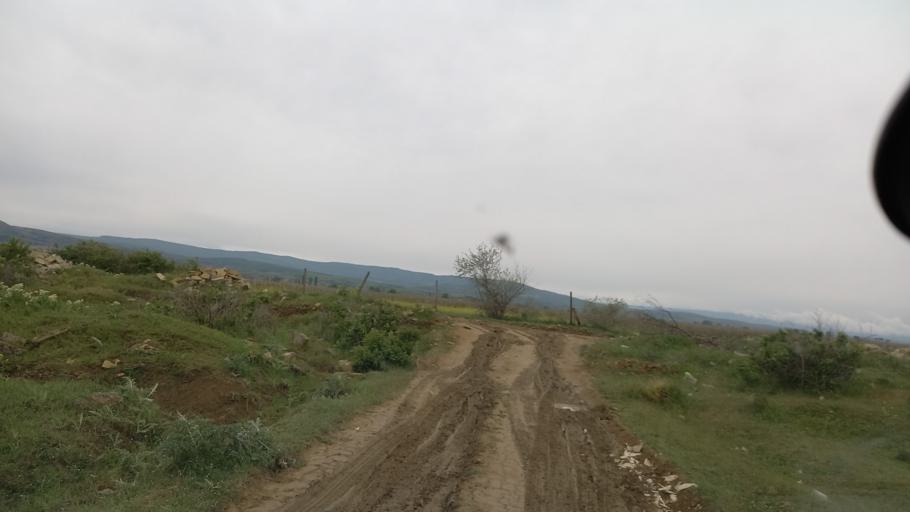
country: RU
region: Dagestan
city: Sabnova
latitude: 42.1176
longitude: 48.2639
